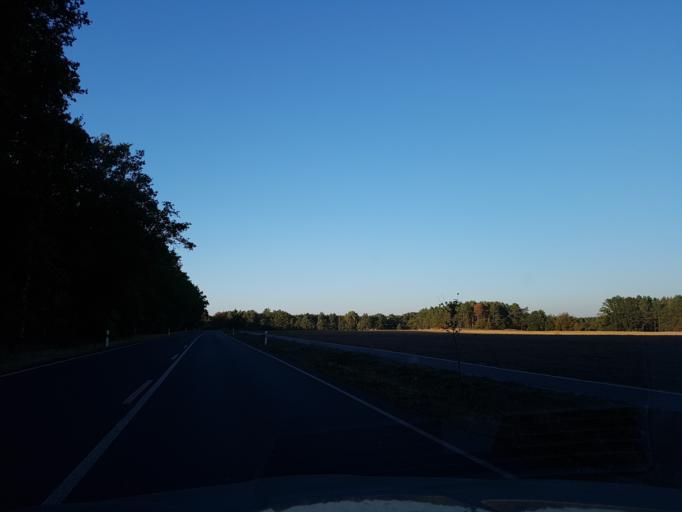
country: DE
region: Brandenburg
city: Bad Liebenwerda
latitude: 51.5358
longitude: 13.3968
